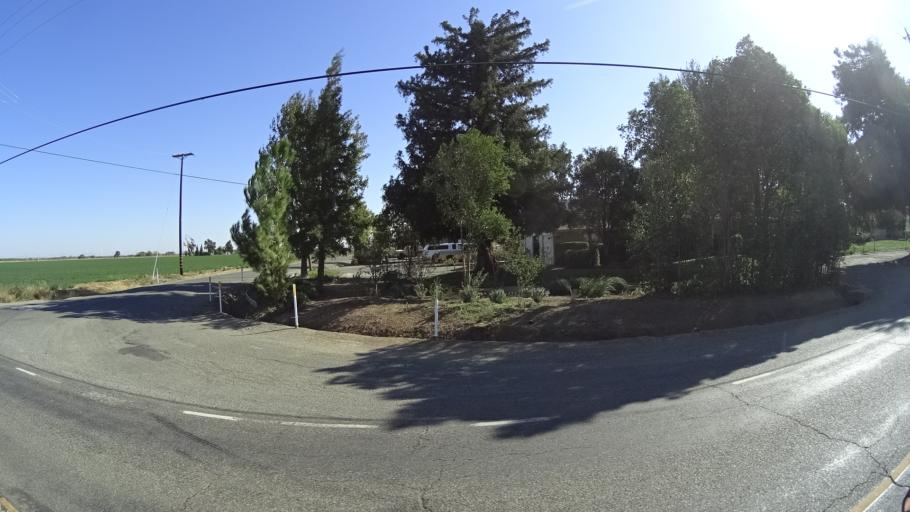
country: US
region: California
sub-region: Yolo County
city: Cottonwood
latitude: 38.6603
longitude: -121.9710
